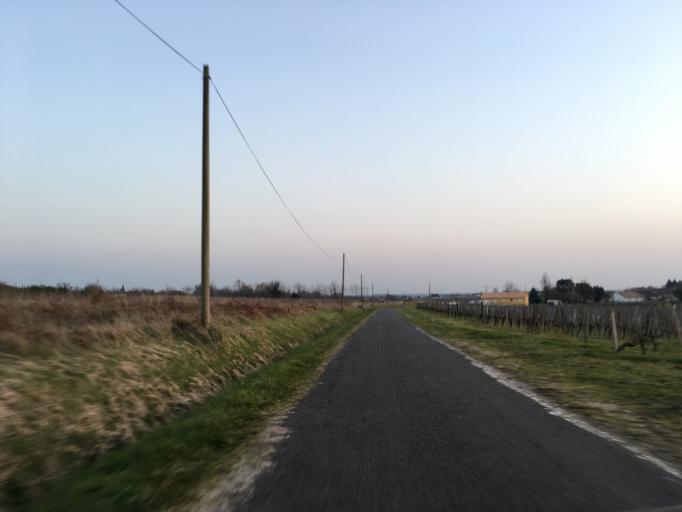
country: FR
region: Aquitaine
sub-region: Departement de la Gironde
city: Saint-Ciers-sur-Gironde
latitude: 45.3020
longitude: -0.6049
